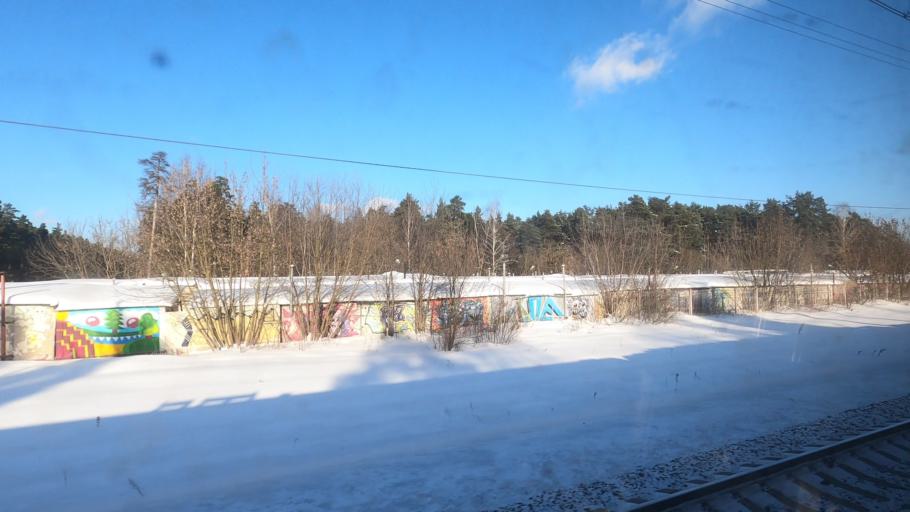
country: RU
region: Moskovskaya
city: Zarya
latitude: 55.7542
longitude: 38.1109
